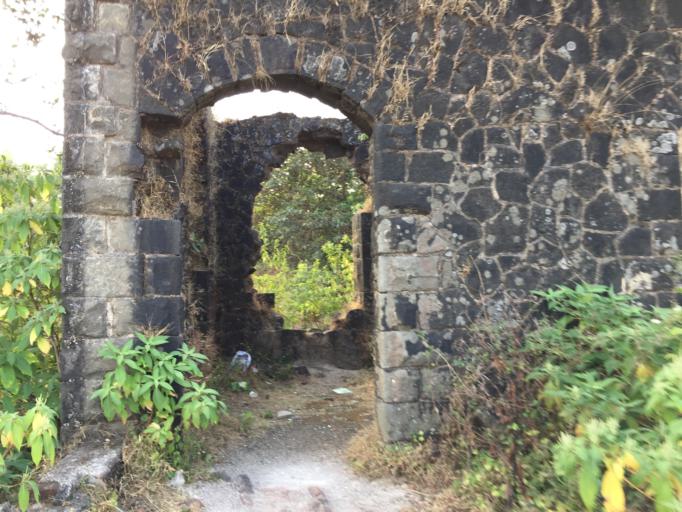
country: IN
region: Maharashtra
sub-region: Pune Division
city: Lonavla
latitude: 18.7739
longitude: 73.4090
